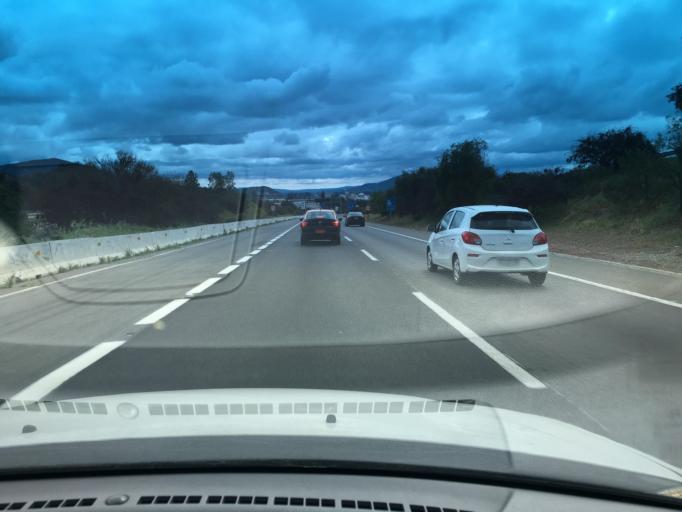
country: CL
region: Santiago Metropolitan
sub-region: Provincia de Melipilla
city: Melipilla
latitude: -33.3757
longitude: -71.2886
